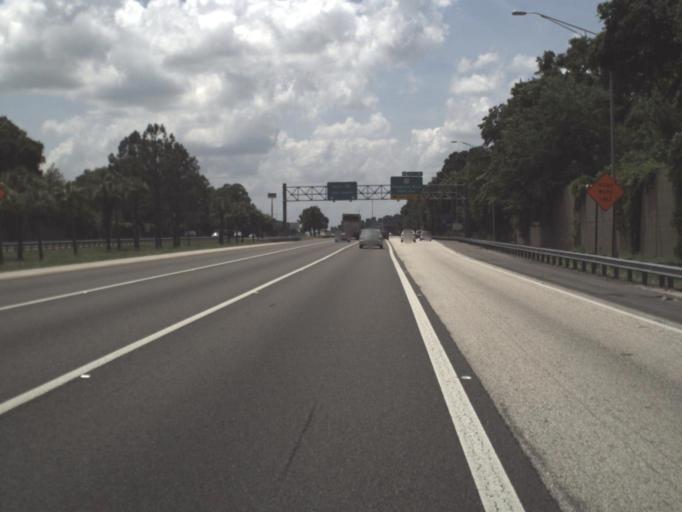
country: US
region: Florida
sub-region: Clay County
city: Orange Park
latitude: 30.1916
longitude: -81.6932
